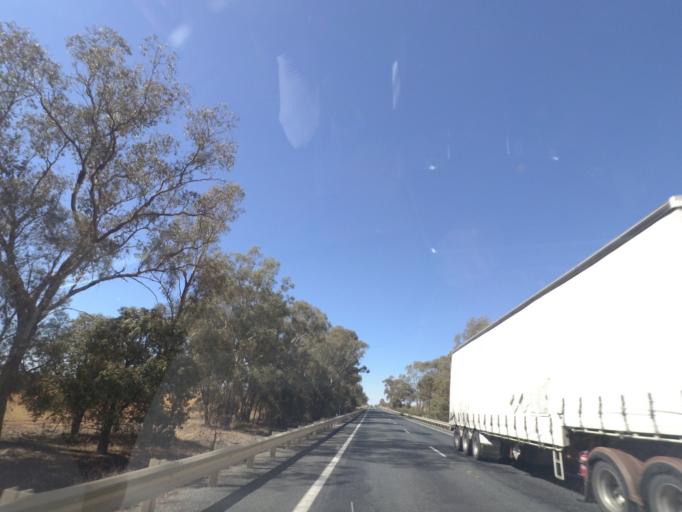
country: AU
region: New South Wales
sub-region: Bland
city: West Wyalong
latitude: -34.1758
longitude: 147.1143
